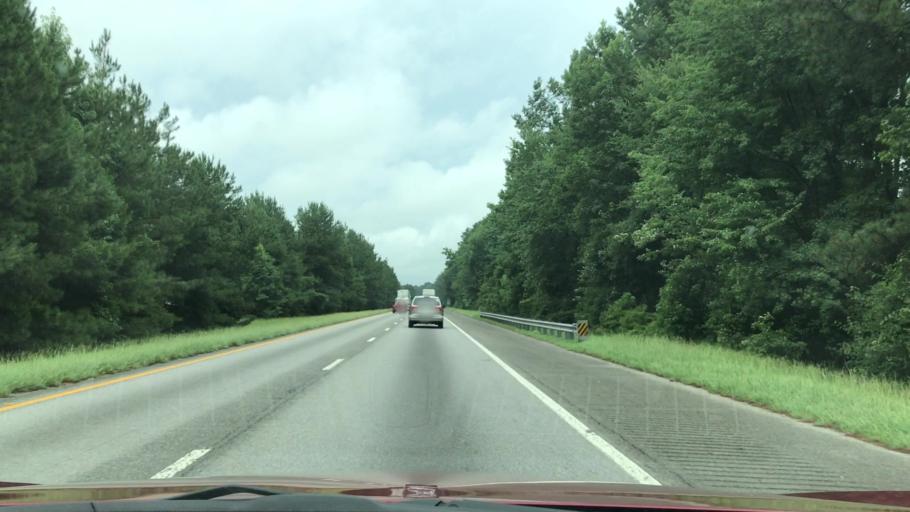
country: US
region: South Carolina
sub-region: Orangeburg County
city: Brookdale
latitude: 33.4053
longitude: -80.6570
